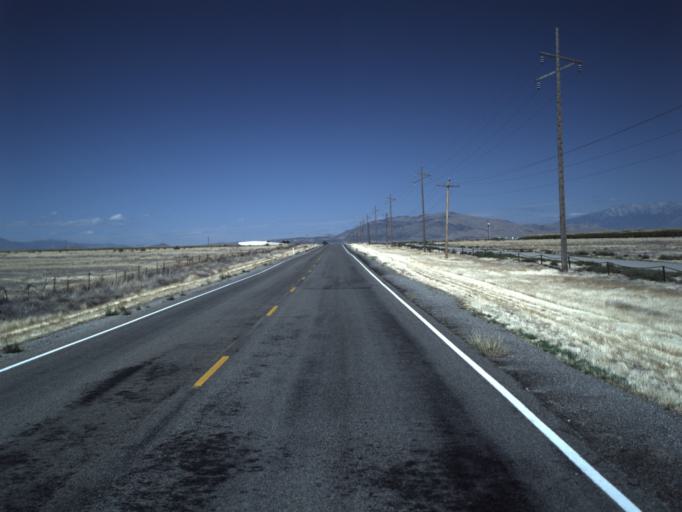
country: US
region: Utah
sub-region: Utah County
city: Genola
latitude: 39.9955
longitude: -111.9576
